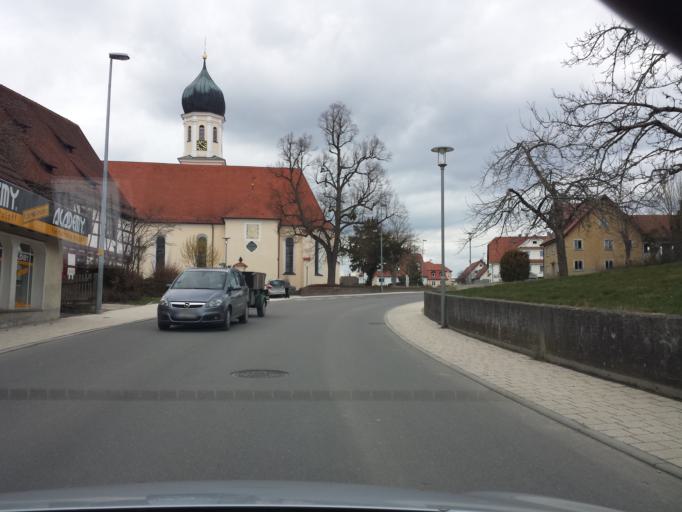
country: DE
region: Baden-Wuerttemberg
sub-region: Tuebingen Region
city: Schwendi
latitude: 48.1782
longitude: 9.9752
